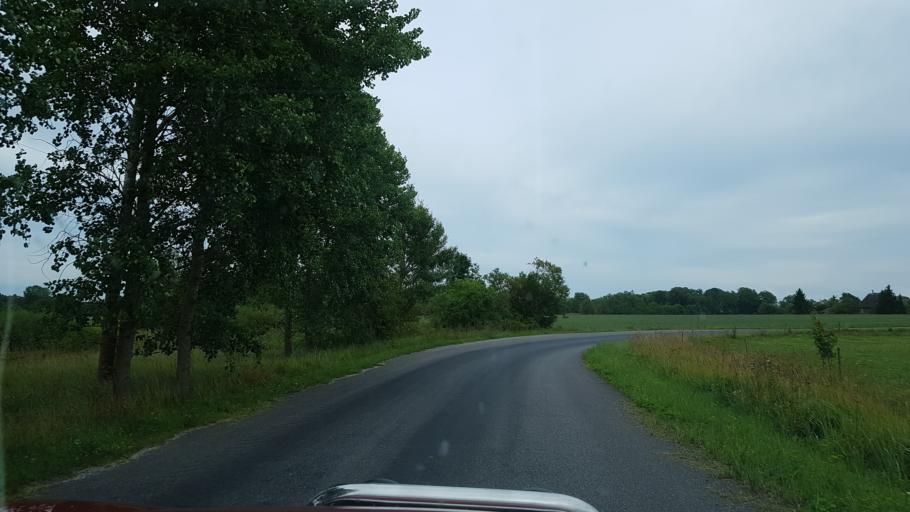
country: EE
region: Laeaene
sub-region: Lihula vald
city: Lihula
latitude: 58.8235
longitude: 23.8247
